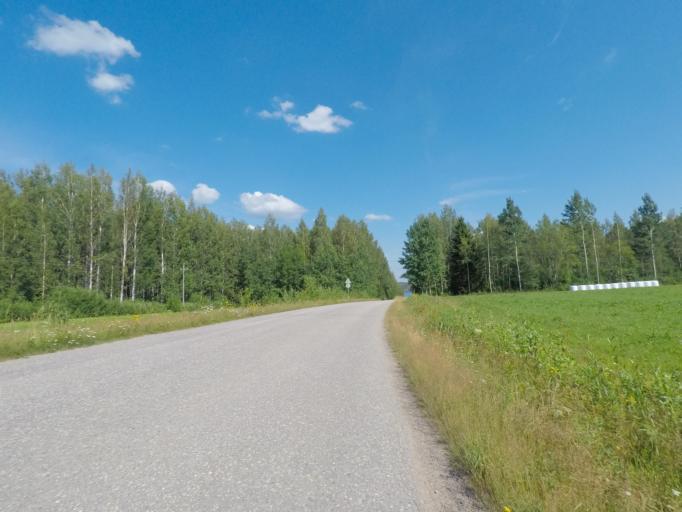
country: FI
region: Southern Savonia
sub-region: Mikkeli
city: Puumala
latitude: 61.4510
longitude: 28.1597
